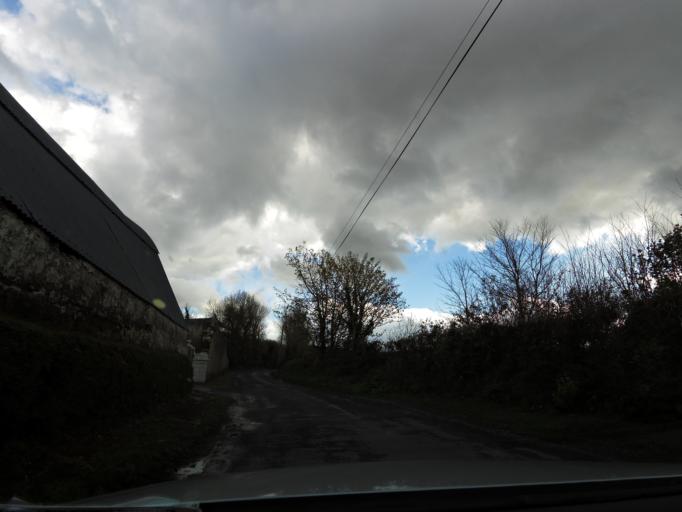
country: IE
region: Leinster
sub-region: Laois
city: Rathdowney
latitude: 52.8160
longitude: -7.4730
